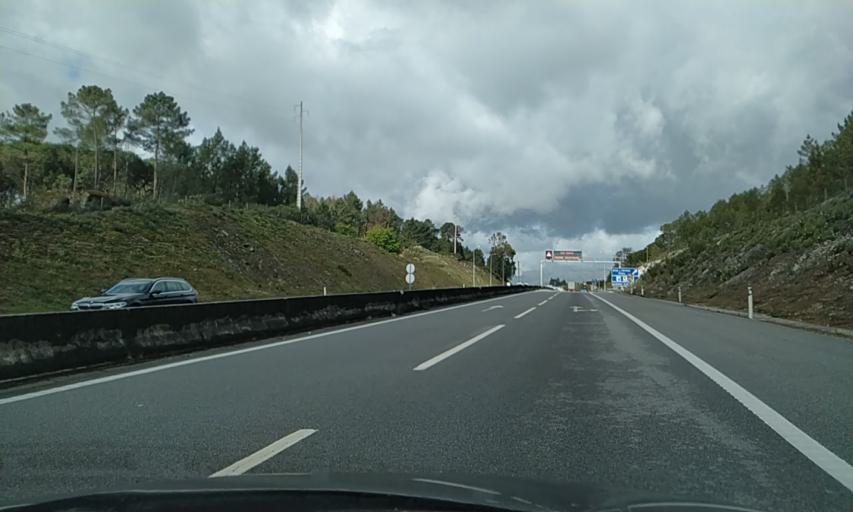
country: PT
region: Viseu
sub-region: Viseu
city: Viseu
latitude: 40.6237
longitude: -7.9257
